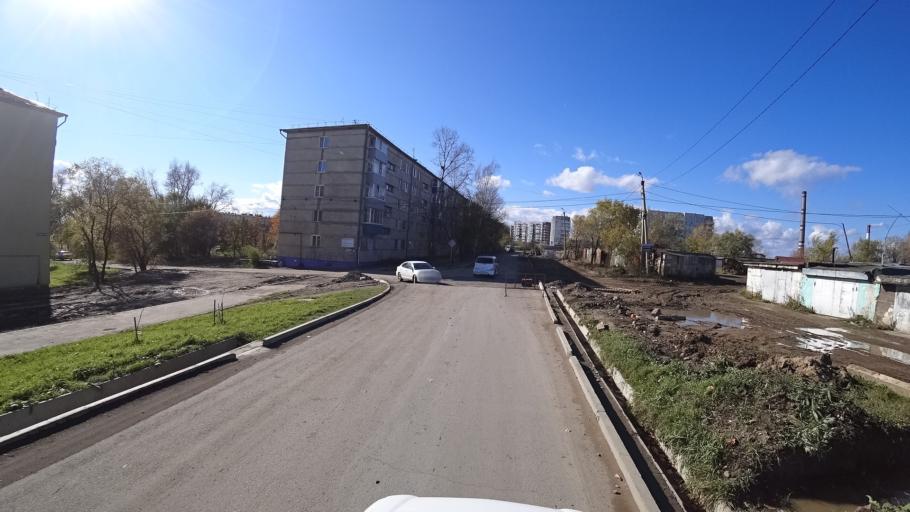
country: RU
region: Khabarovsk Krai
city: Amursk
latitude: 50.2180
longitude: 136.8980
